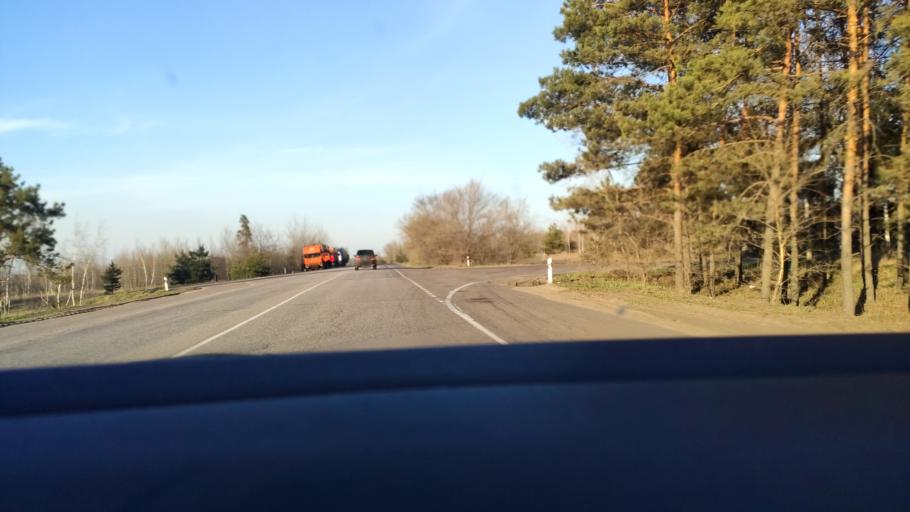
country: RU
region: Voronezj
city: Kolodeznyy
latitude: 51.3687
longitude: 39.2015
